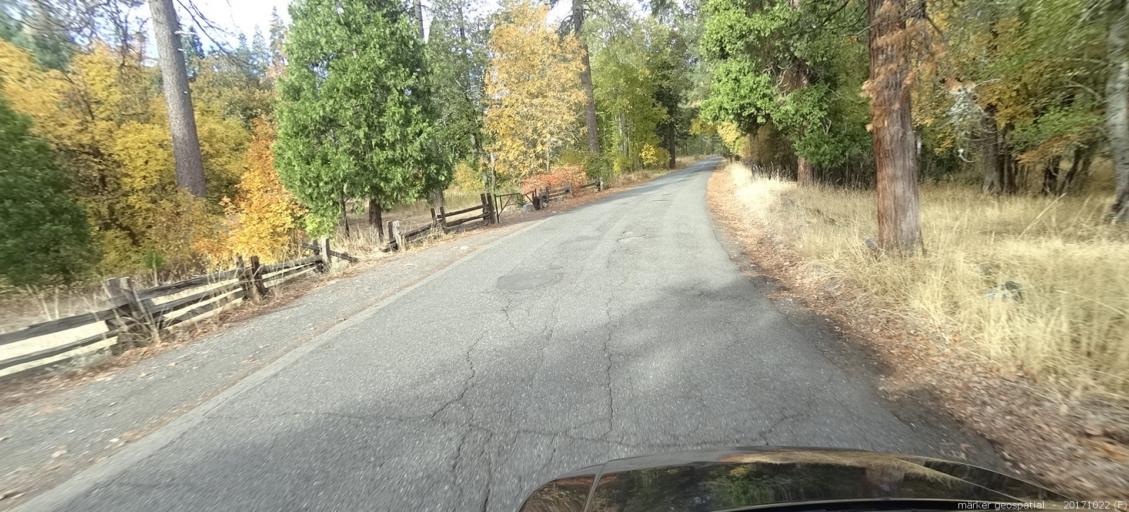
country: US
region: California
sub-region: Siskiyou County
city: Dunsmuir
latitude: 41.1524
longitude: -122.3398
